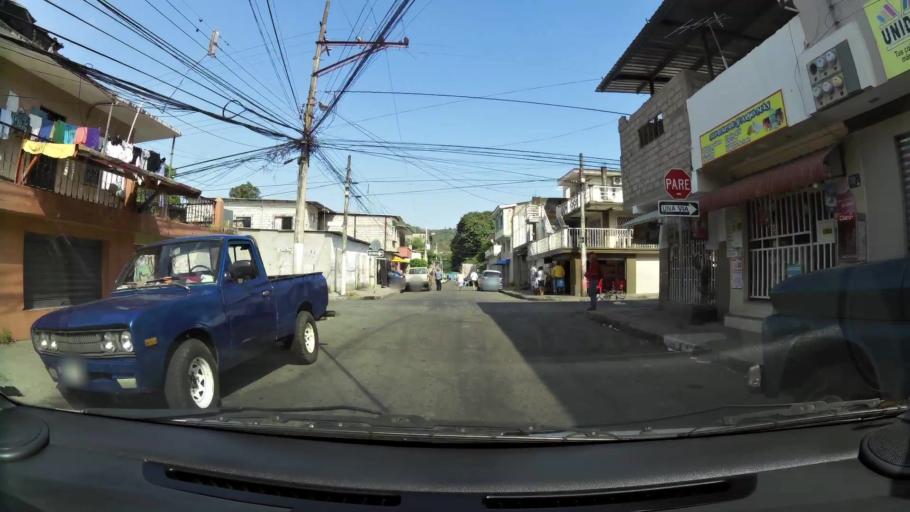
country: EC
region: Guayas
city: Guayaquil
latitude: -2.1605
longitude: -79.9362
